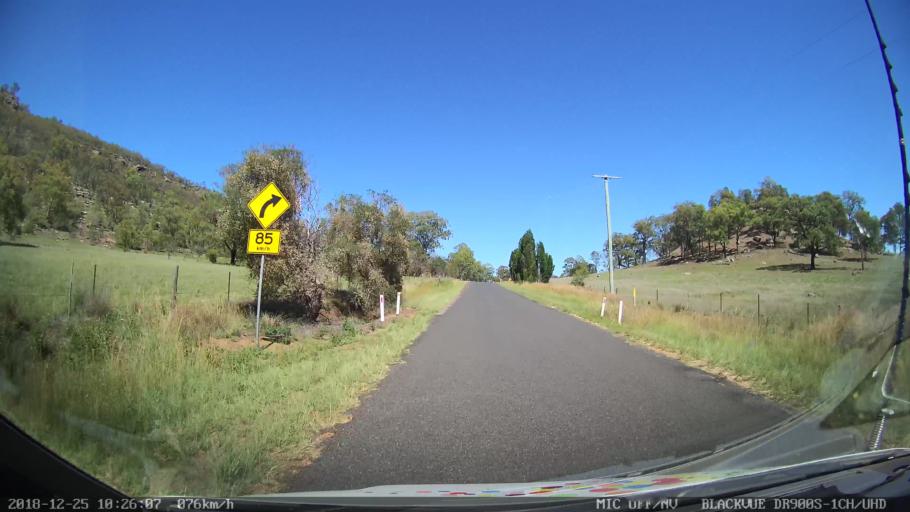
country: AU
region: New South Wales
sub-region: Muswellbrook
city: Denman
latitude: -32.3910
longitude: 150.4894
